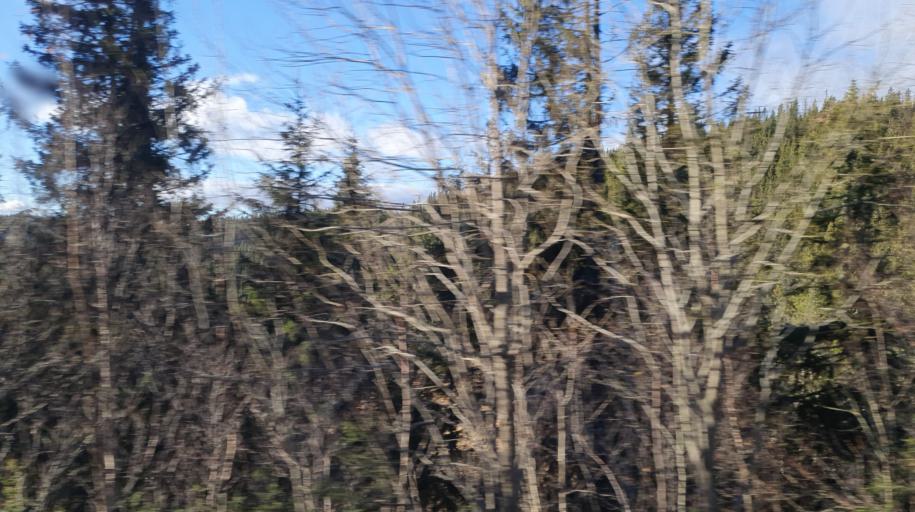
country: NO
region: Buskerud
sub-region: Krodsherad
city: Noresund
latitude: 60.2218
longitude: 9.5326
